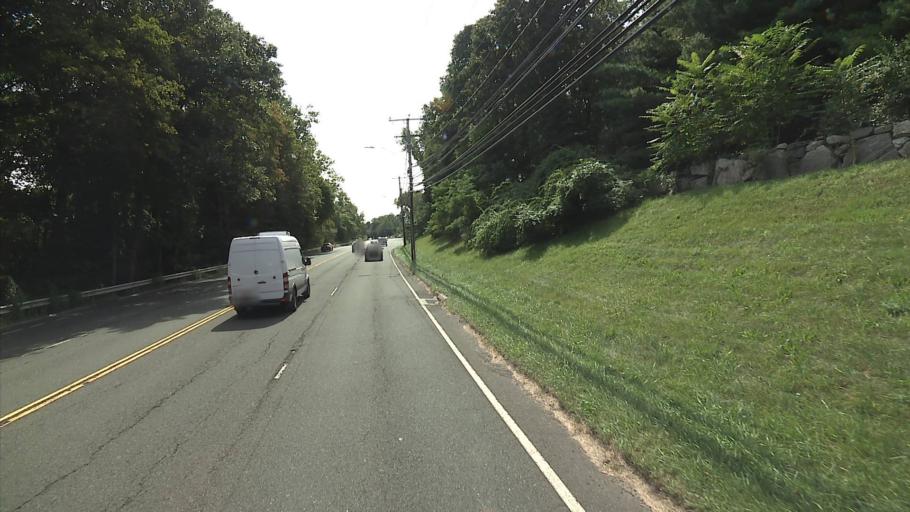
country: US
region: Connecticut
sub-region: Fairfield County
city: Stamford
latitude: 41.0914
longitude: -73.5611
